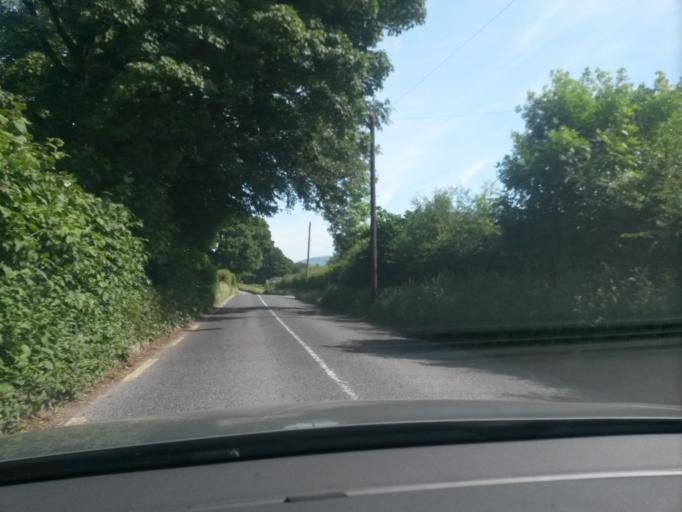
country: IE
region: Leinster
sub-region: Wicklow
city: Blessington
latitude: 53.1752
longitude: -6.5570
